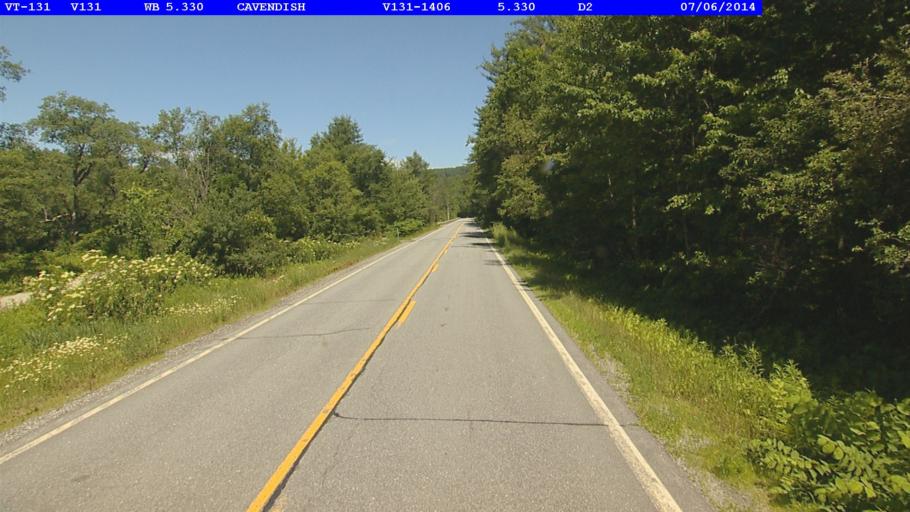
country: US
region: Vermont
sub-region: Windsor County
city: Springfield
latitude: 43.3989
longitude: -72.5688
